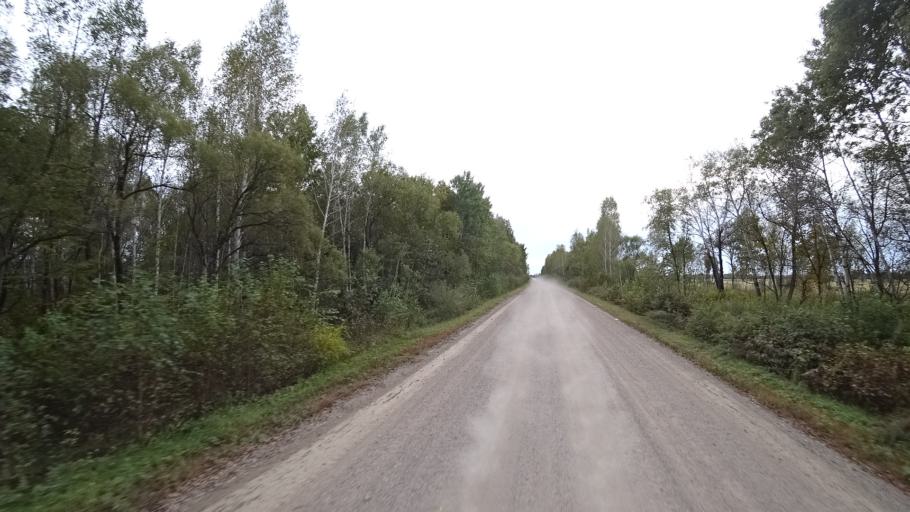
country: RU
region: Amur
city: Arkhara
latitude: 49.3814
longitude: 130.2173
